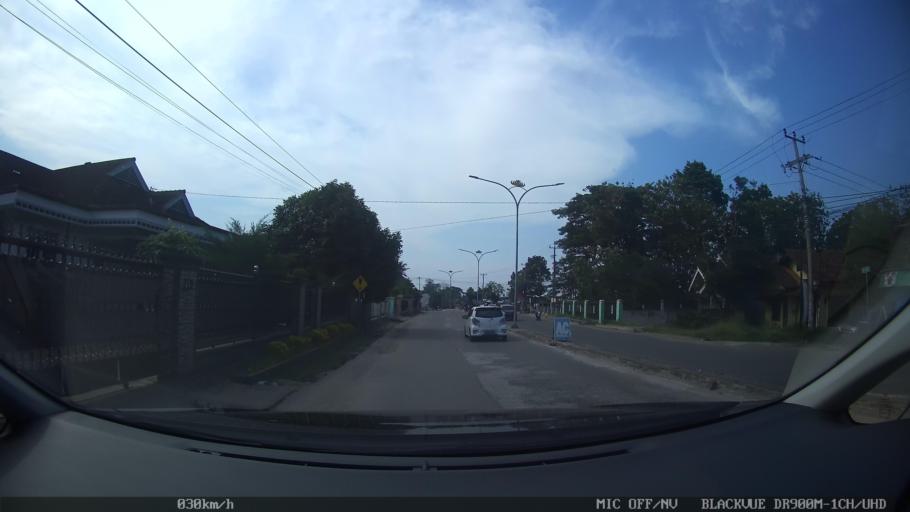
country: ID
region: Lampung
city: Kedaton
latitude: -5.3837
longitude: 105.2217
